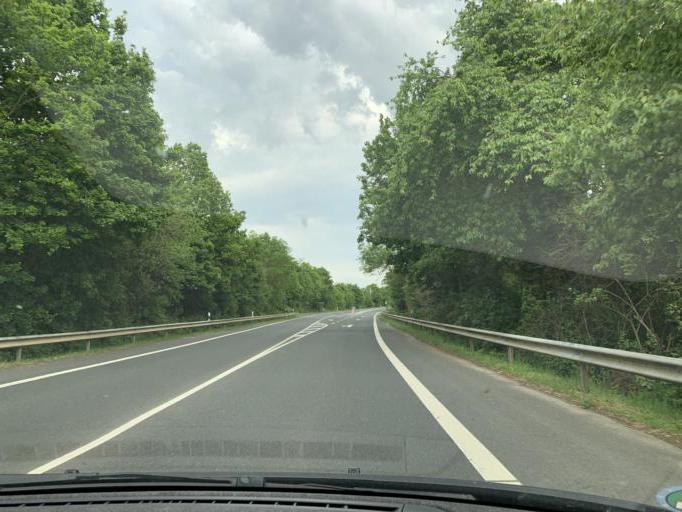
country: DE
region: North Rhine-Westphalia
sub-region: Regierungsbezirk Koln
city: Norvenich
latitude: 50.7550
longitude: 6.6415
